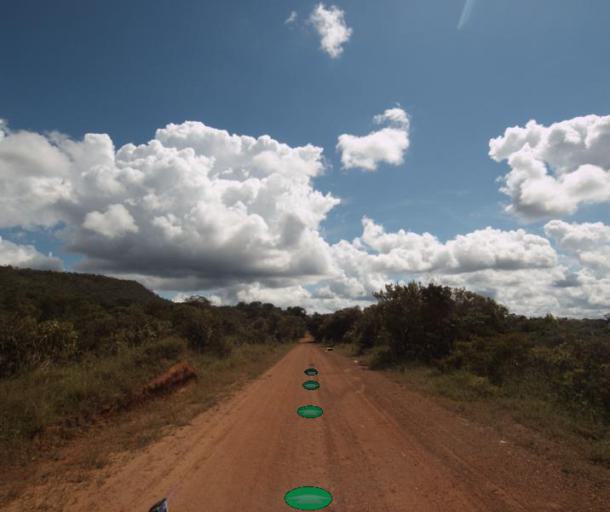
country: BR
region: Goias
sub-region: Pirenopolis
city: Pirenopolis
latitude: -15.7806
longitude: -48.8361
